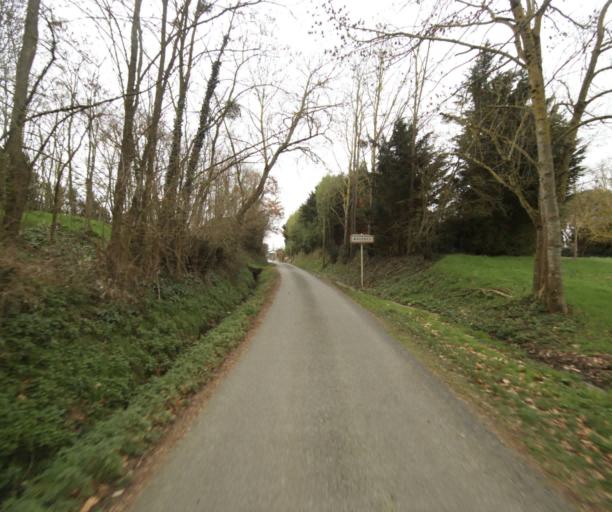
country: FR
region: Midi-Pyrenees
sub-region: Departement de l'Ariege
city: Mazeres
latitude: 43.2502
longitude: 1.6702
